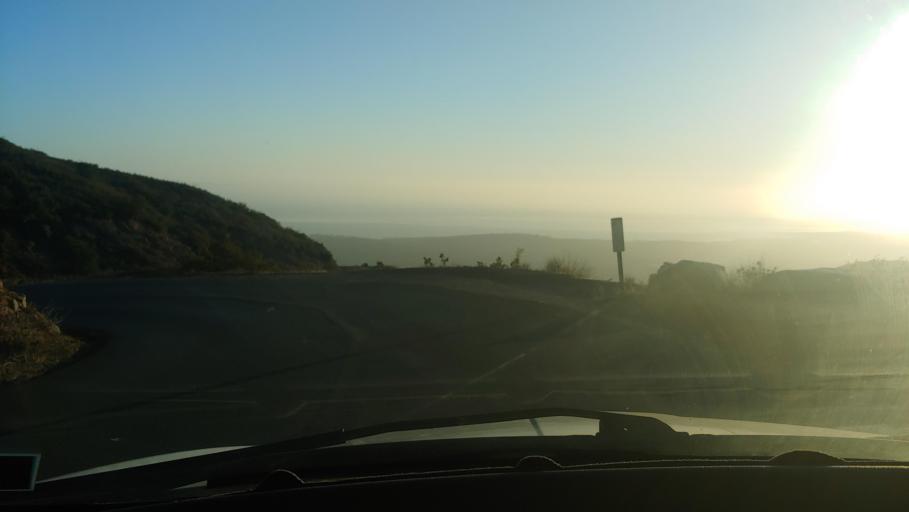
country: US
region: California
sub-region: Santa Barbara County
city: Mission Canyon
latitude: 34.4762
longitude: -119.6796
